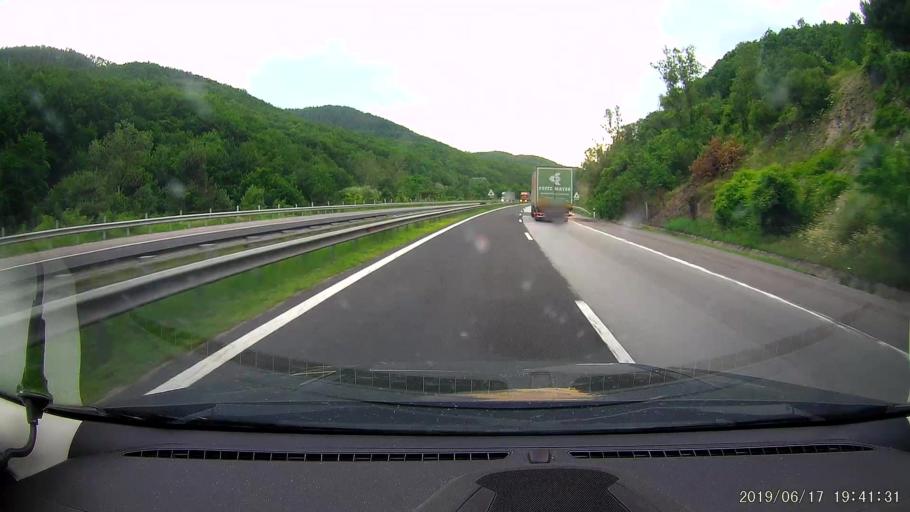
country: BG
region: Sofiya
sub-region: Obshtina Ikhtiman
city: Ikhtiman
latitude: 42.3459
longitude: 23.9331
